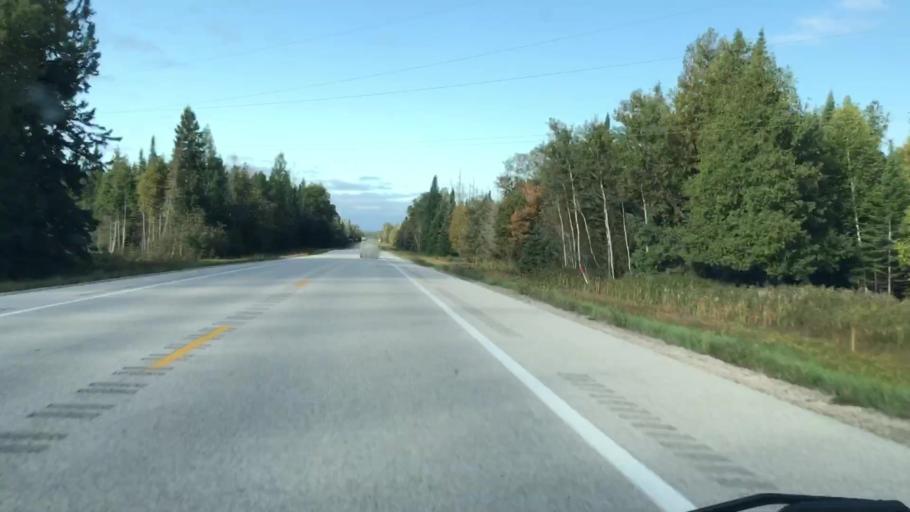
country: US
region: Michigan
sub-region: Luce County
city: Newberry
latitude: 46.3293
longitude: -85.1558
